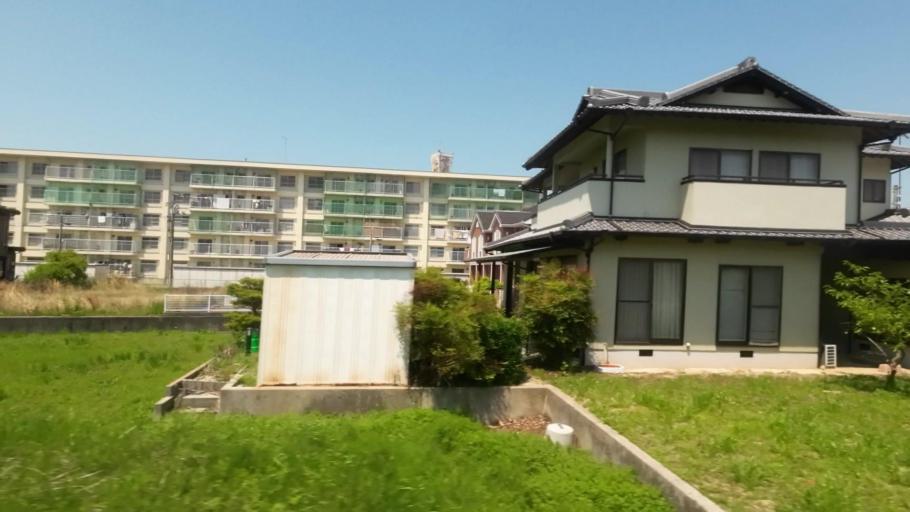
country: JP
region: Ehime
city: Hojo
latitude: 33.9448
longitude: 132.7714
